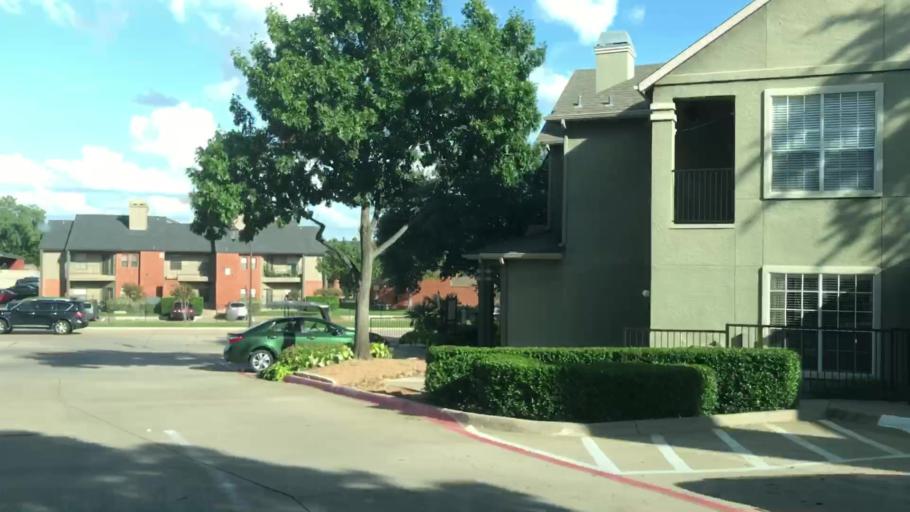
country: US
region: Texas
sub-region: Dallas County
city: Coppell
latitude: 32.9428
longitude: -96.9561
